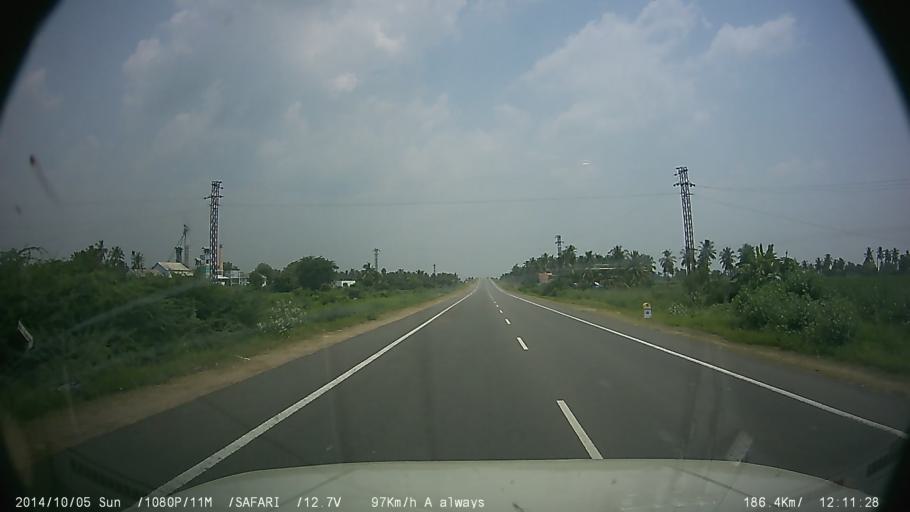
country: IN
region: Tamil Nadu
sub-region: Villupuram
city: Kallakkurichchi
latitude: 11.7200
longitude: 78.9605
